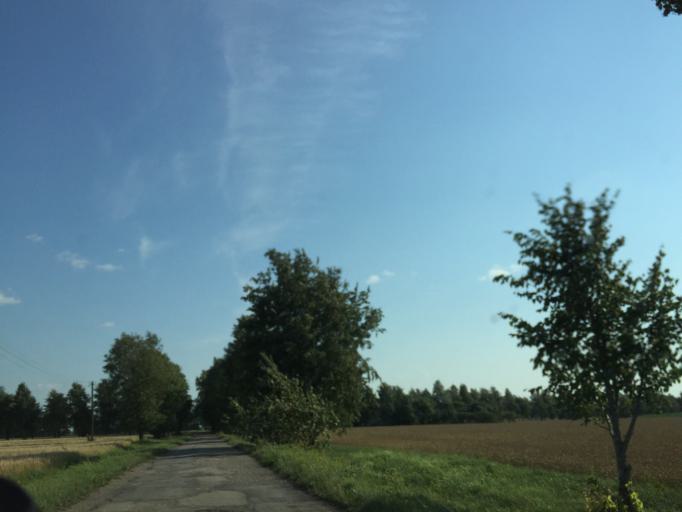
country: LV
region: Jelgava
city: Jelgava
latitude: 56.4523
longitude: 23.6806
